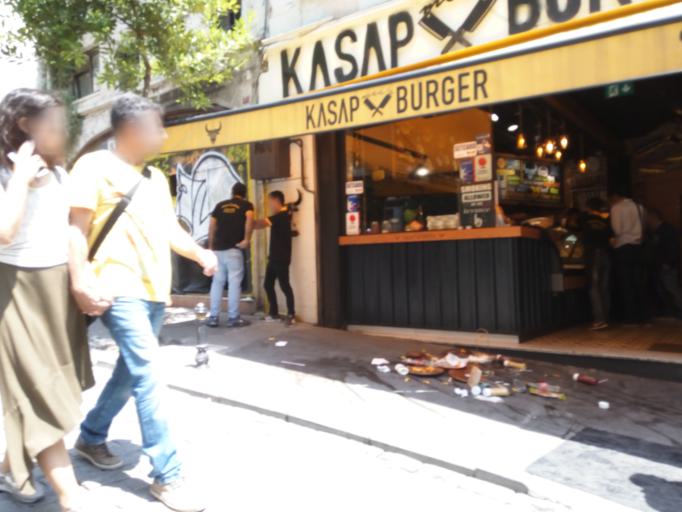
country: TR
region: Istanbul
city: Eminoenue
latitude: 41.0279
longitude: 28.9745
